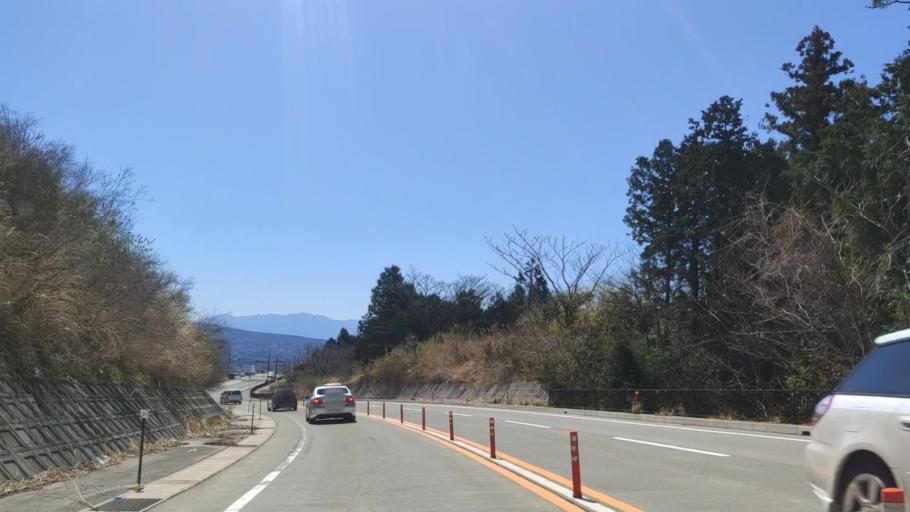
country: JP
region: Kanagawa
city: Hakone
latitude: 35.1533
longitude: 138.9900
